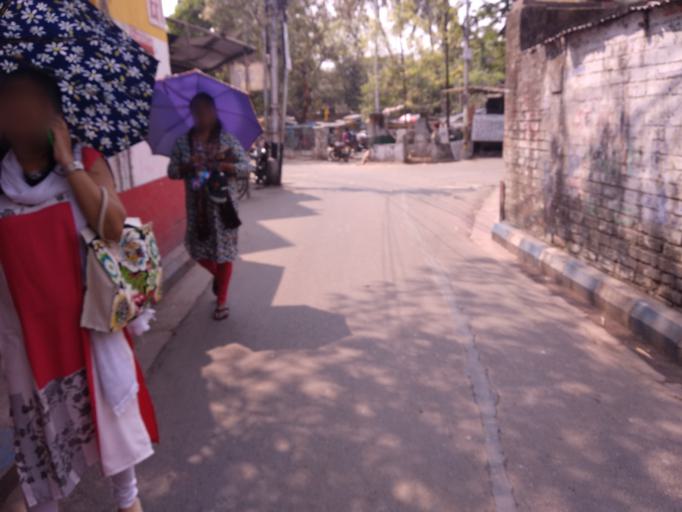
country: IN
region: West Bengal
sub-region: Kolkata
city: Kolkata
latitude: 22.5052
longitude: 88.3763
